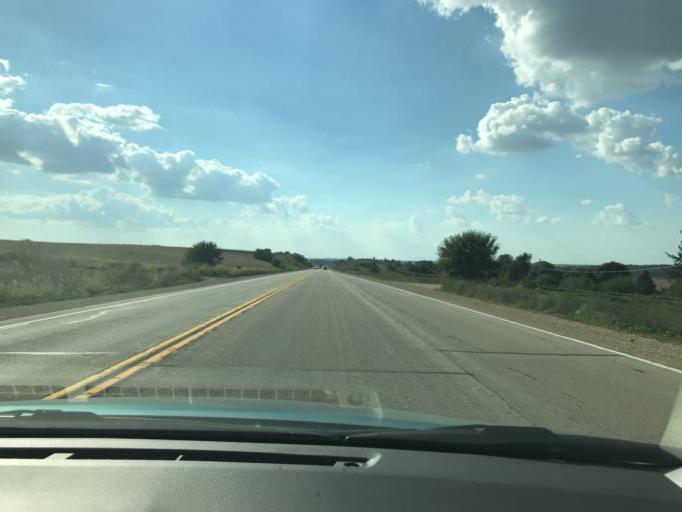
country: US
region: Wisconsin
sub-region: Green County
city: Brodhead
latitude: 42.5883
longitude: -89.4537
